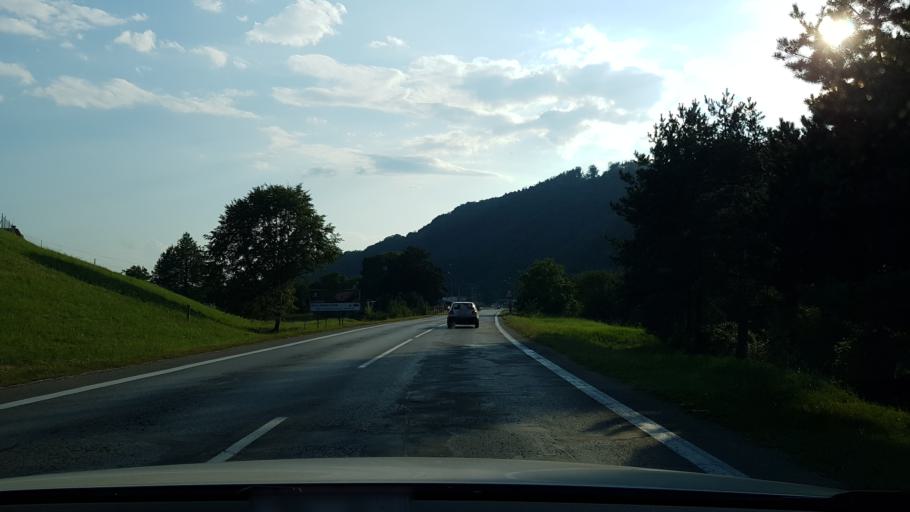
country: SK
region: Trenciansky
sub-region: Okres Povazska Bystrica
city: Povazska Bystrica
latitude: 49.1348
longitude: 18.4548
